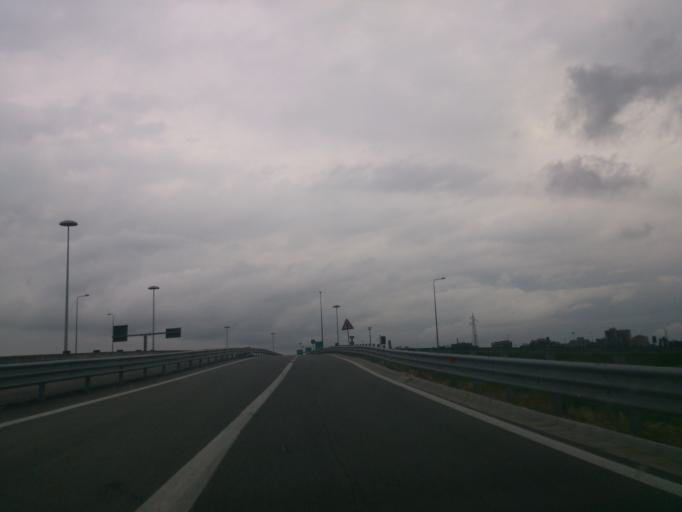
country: IT
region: Lombardy
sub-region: Citta metropolitana di Milano
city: San Donato Milanese
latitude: 45.4362
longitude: 9.2519
